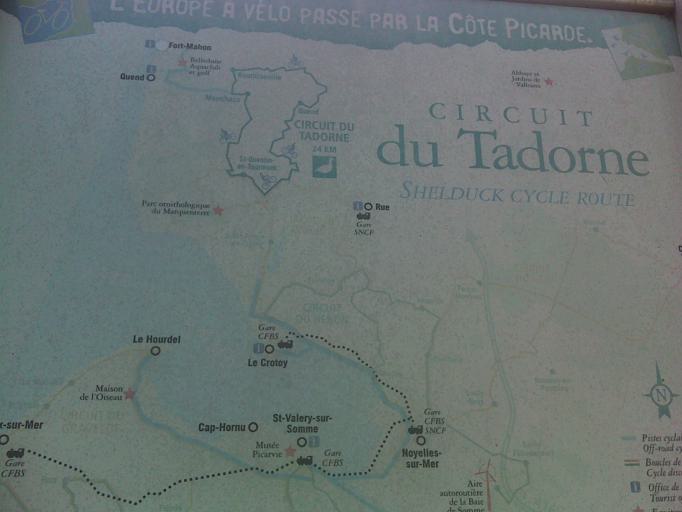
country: FR
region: Picardie
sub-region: Departement de la Somme
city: Fort-Mahon-Plage
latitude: 50.3396
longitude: 1.5571
